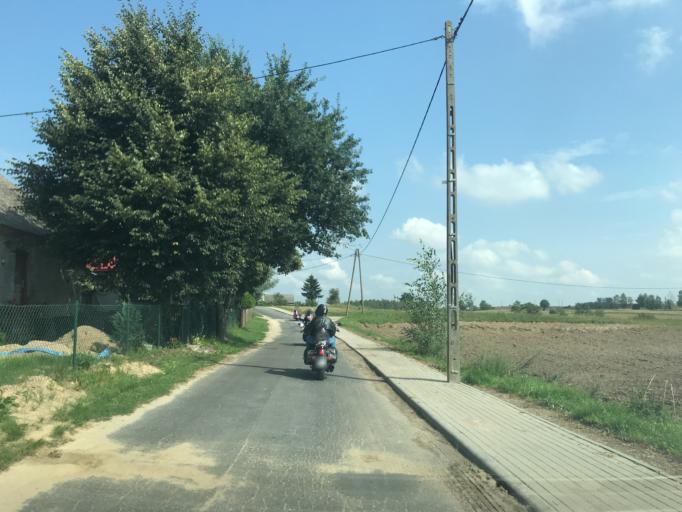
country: PL
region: Warmian-Masurian Voivodeship
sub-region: Powiat nowomiejski
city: Biskupiec
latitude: 53.4217
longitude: 19.4424
